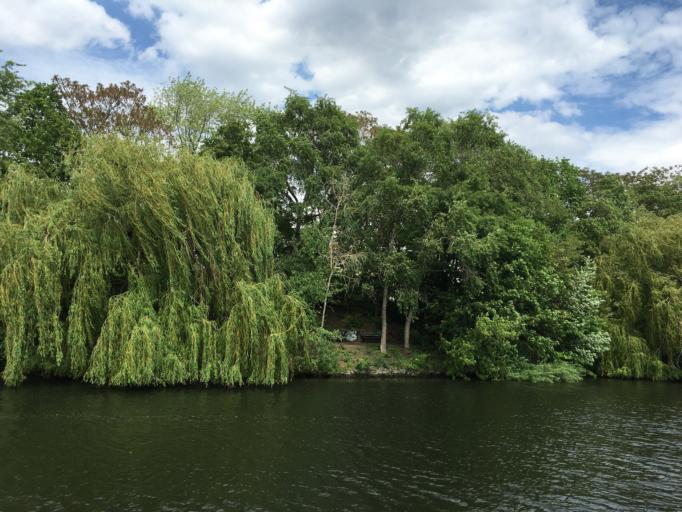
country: DE
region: Berlin
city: Hansaviertel
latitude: 52.5175
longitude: 13.3307
